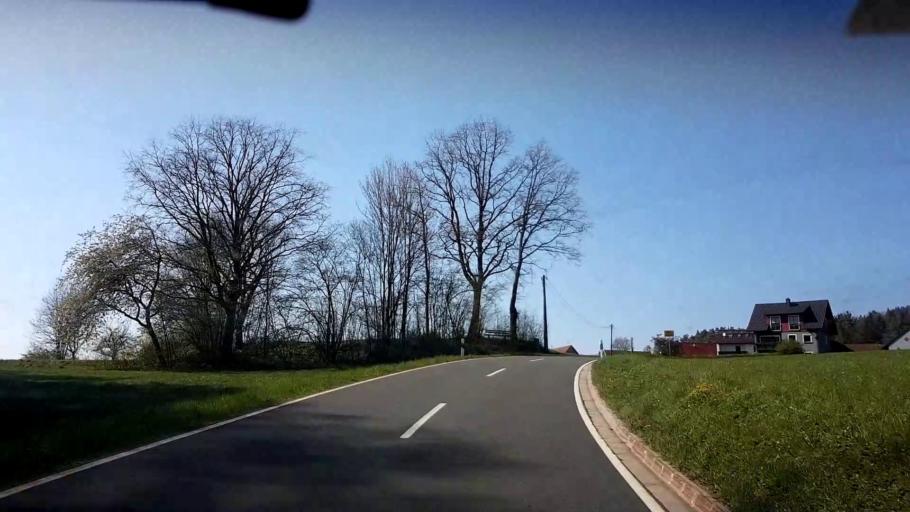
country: DE
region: Bavaria
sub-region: Upper Franconia
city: Pottenstein
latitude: 49.7976
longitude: 11.4057
